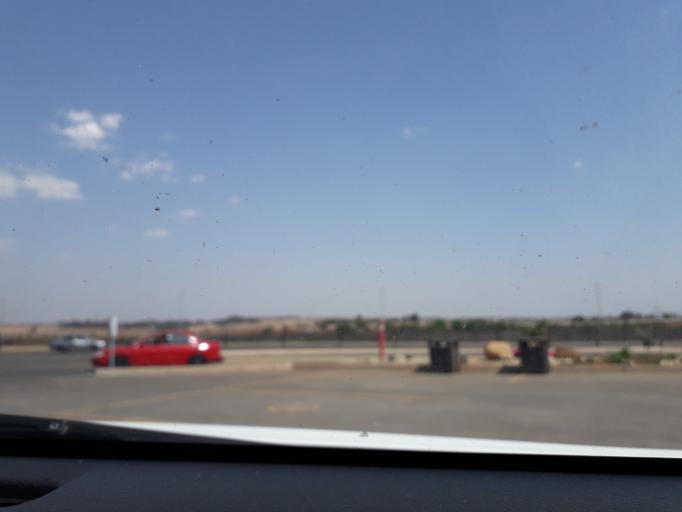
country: ZA
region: Gauteng
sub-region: Ekurhuleni Metropolitan Municipality
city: Tembisa
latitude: -26.0359
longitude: 28.2570
